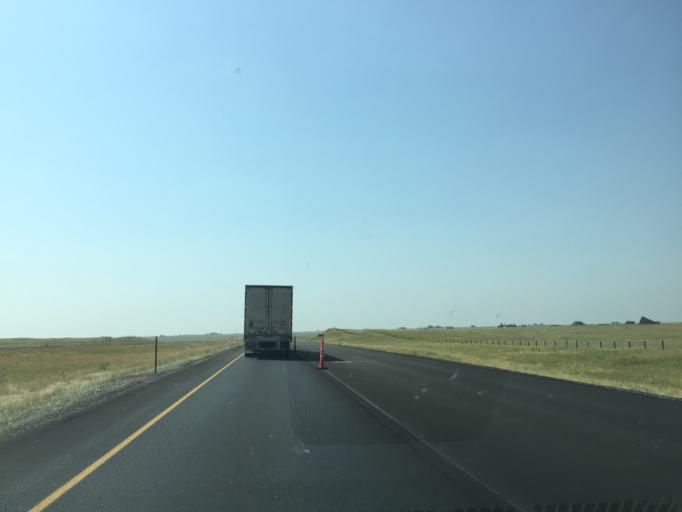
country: US
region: Wyoming
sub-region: Laramie County
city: Ranchettes
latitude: 41.3169
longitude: -104.8598
